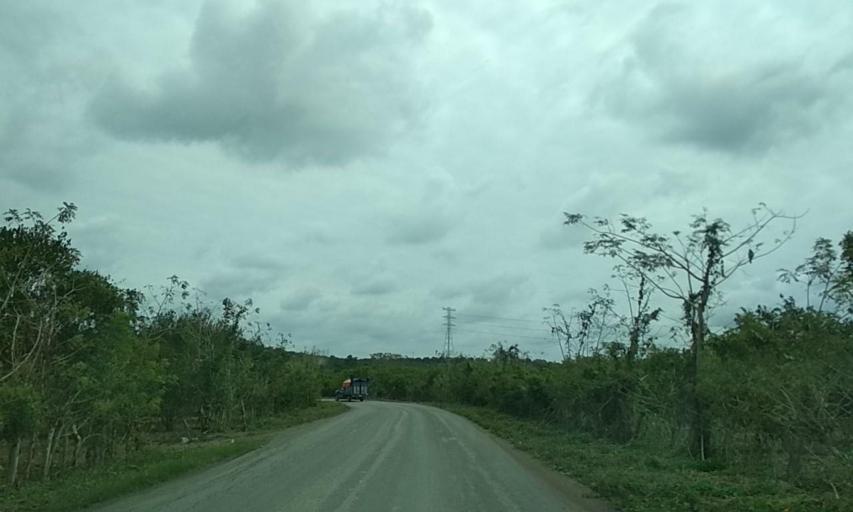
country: MX
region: Veracruz
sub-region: Papantla
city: El Chote
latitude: 20.3515
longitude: -97.3547
